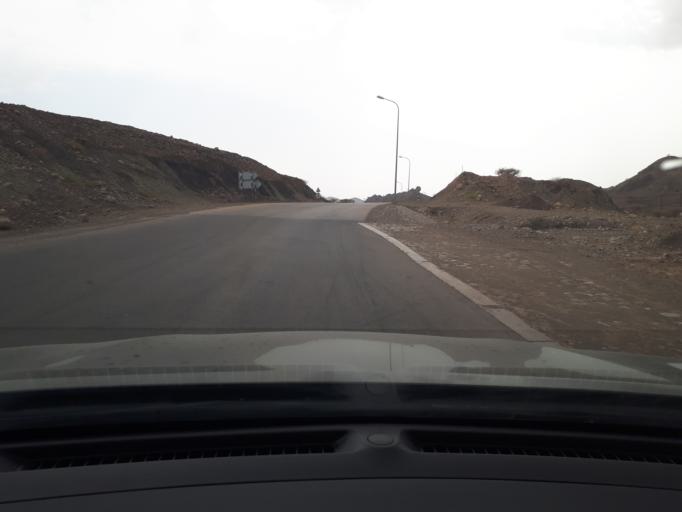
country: OM
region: Ash Sharqiyah
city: Badiyah
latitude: 22.5627
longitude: 59.0327
